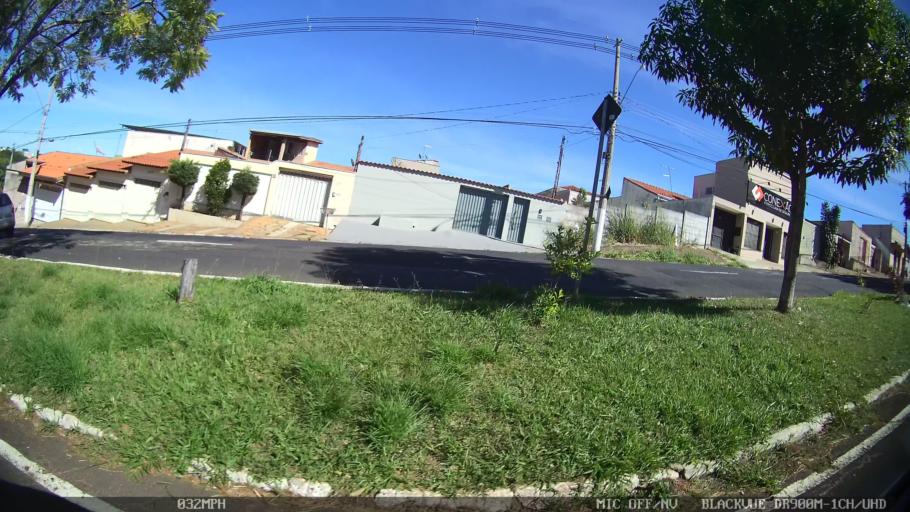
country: BR
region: Sao Paulo
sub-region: Franca
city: Franca
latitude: -20.5488
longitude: -47.3730
